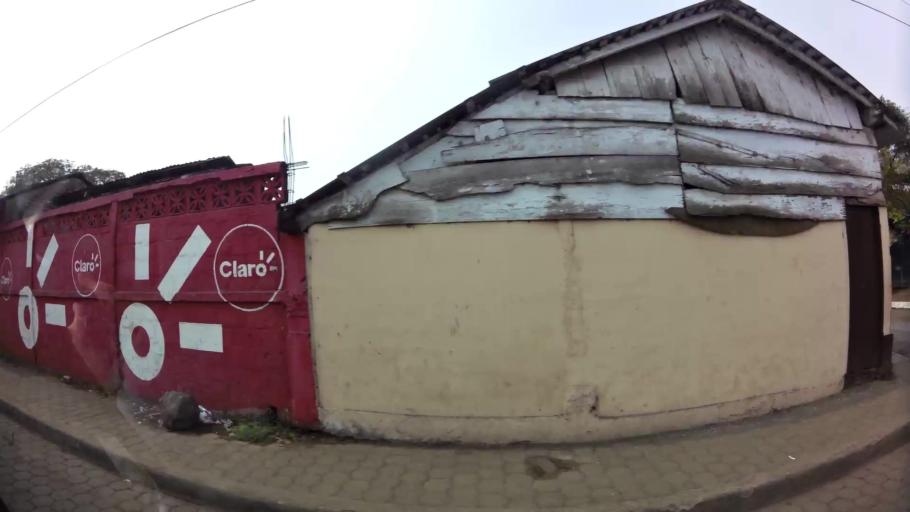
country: NI
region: Chinandega
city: Chinandega
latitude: 12.6300
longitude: -87.1373
